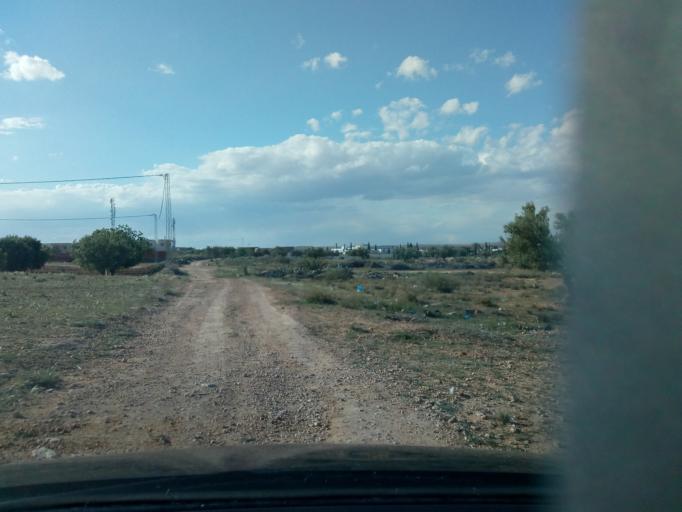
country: TN
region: Safaqis
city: Sfax
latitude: 34.7238
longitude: 10.6112
